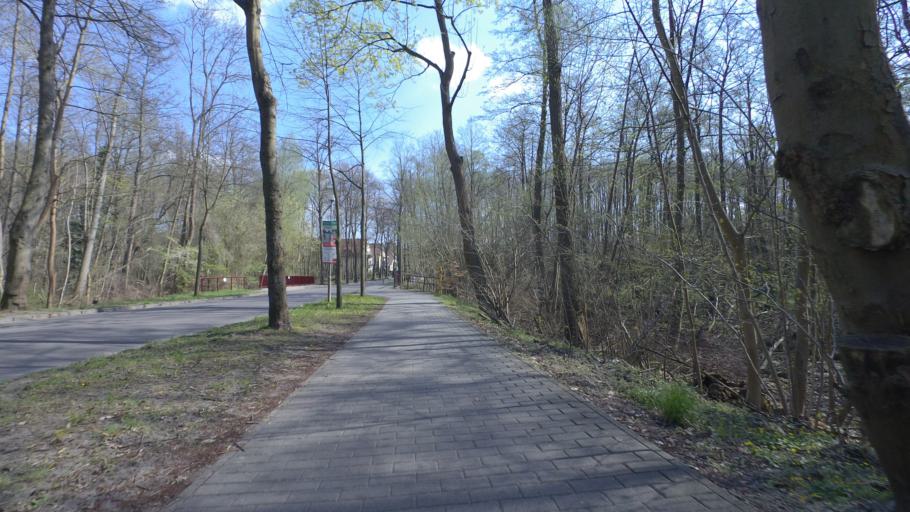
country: DE
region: Brandenburg
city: Rangsdorf
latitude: 52.2883
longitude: 13.4460
